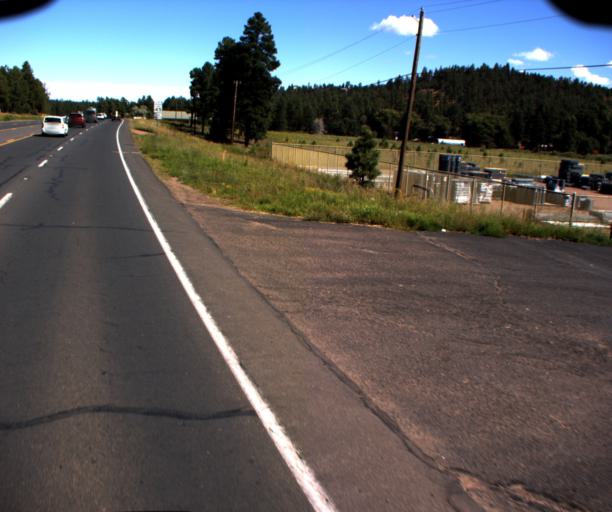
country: US
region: Arizona
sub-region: Navajo County
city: Show Low
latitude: 34.2157
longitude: -110.0287
